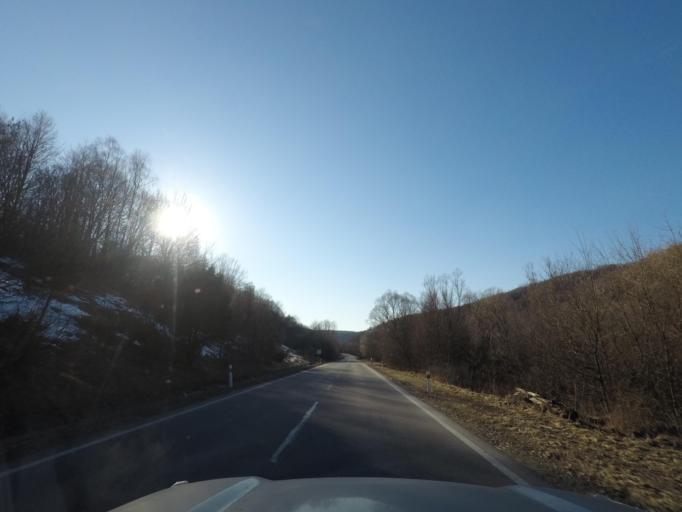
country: SK
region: Presovsky
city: Medzilaborce
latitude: 49.2808
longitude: 21.8369
